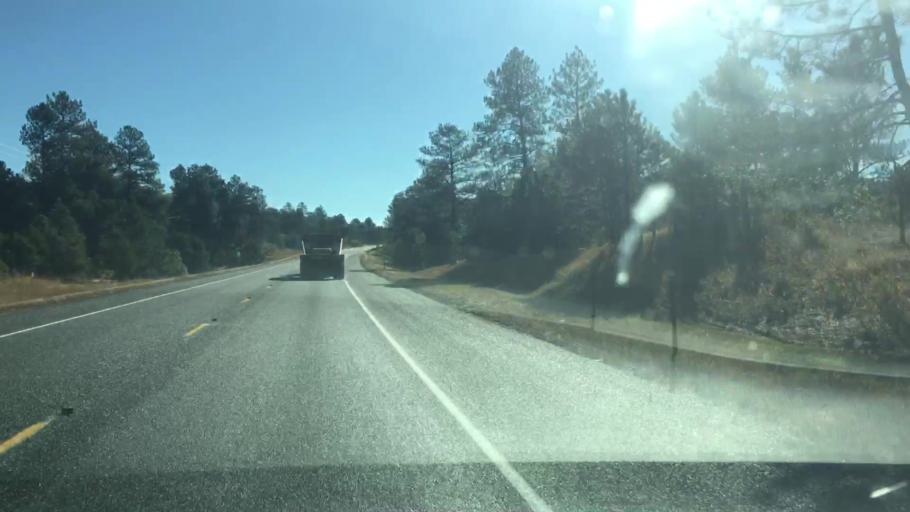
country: US
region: Colorado
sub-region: Elbert County
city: Ponderosa Park
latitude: 39.3779
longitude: -104.6998
